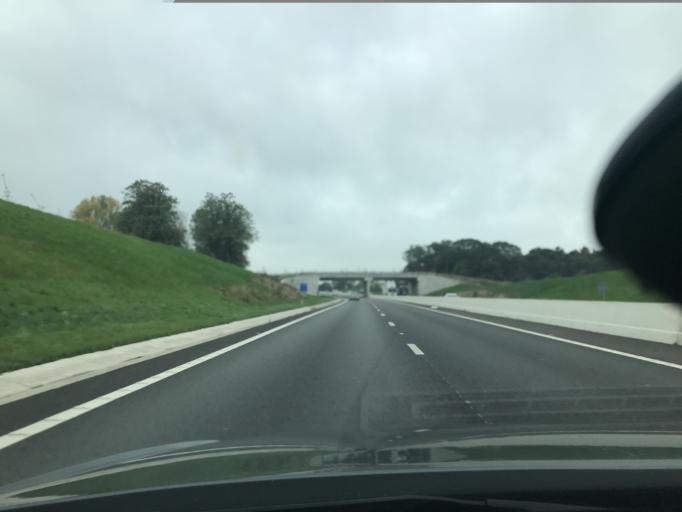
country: GB
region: England
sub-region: Cheshire East
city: Mere
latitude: 53.3343
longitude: -2.4195
